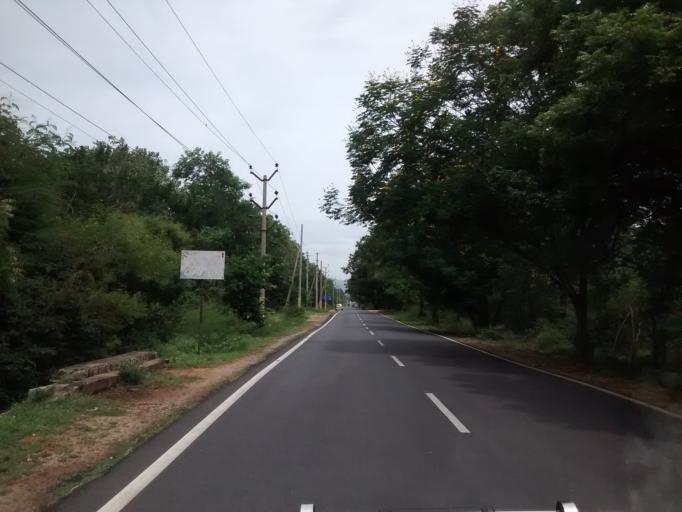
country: IN
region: Andhra Pradesh
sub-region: Chittoor
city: Tirupati
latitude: 13.6316
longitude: 79.3860
